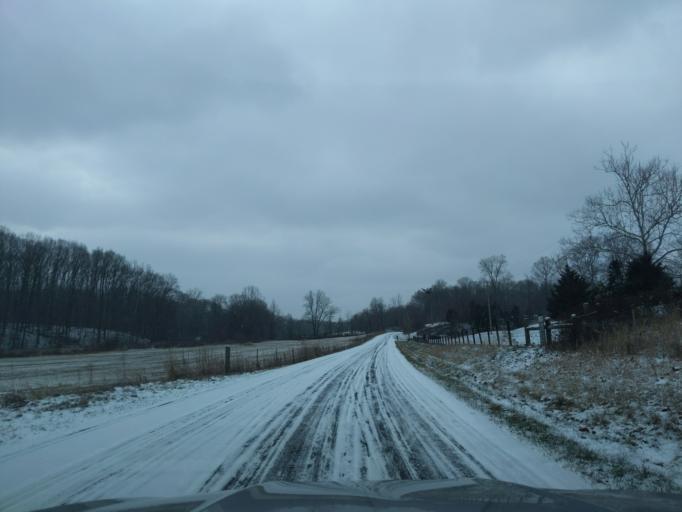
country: US
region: Indiana
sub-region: Decatur County
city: Westport
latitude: 39.2148
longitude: -85.5187
